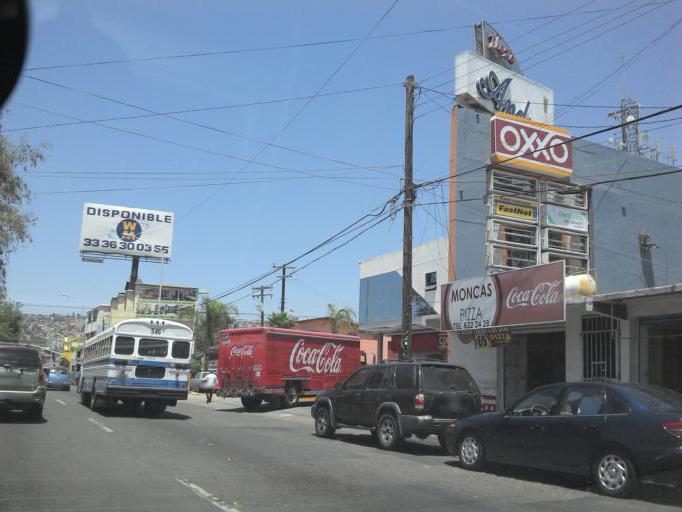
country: MX
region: Baja California
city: Tijuana
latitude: 32.5121
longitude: -116.9871
